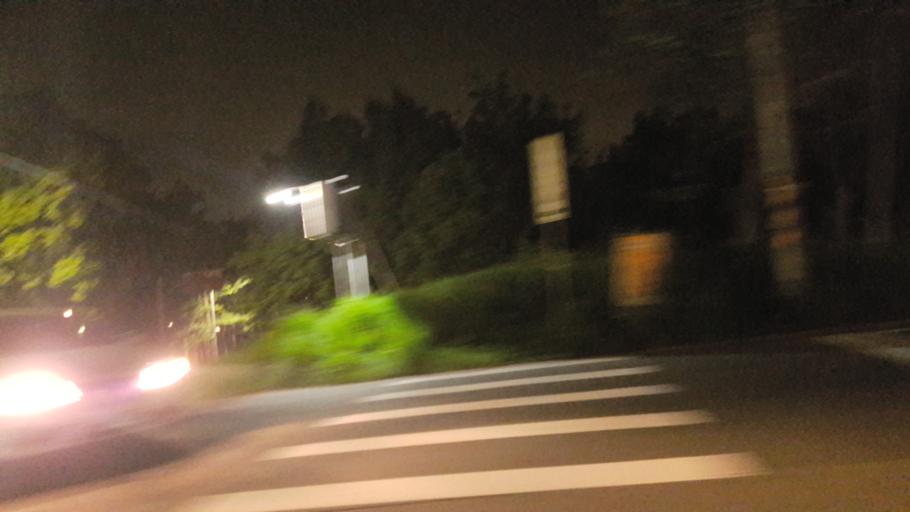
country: TW
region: Taiwan
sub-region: Hsinchu
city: Hsinchu
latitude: 24.7712
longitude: 120.9720
